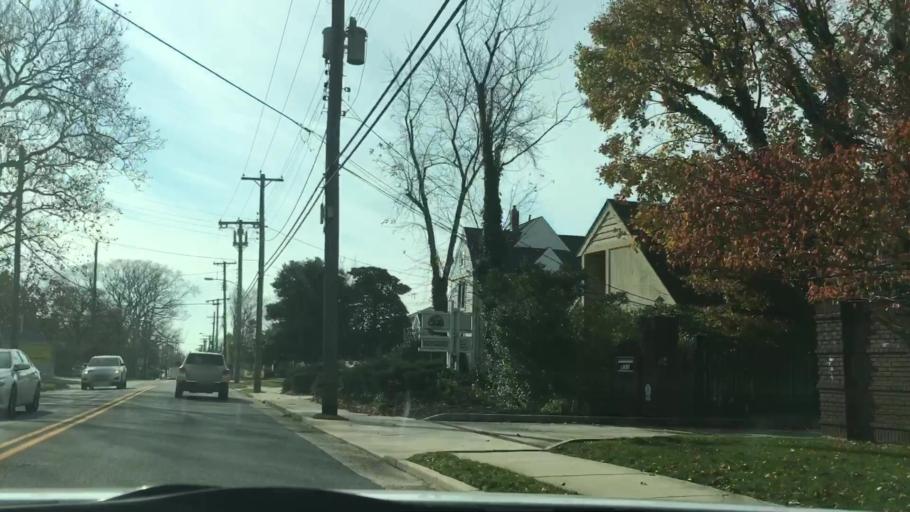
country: US
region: New Jersey
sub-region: Atlantic County
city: Pleasantville
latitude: 39.4028
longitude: -74.5127
